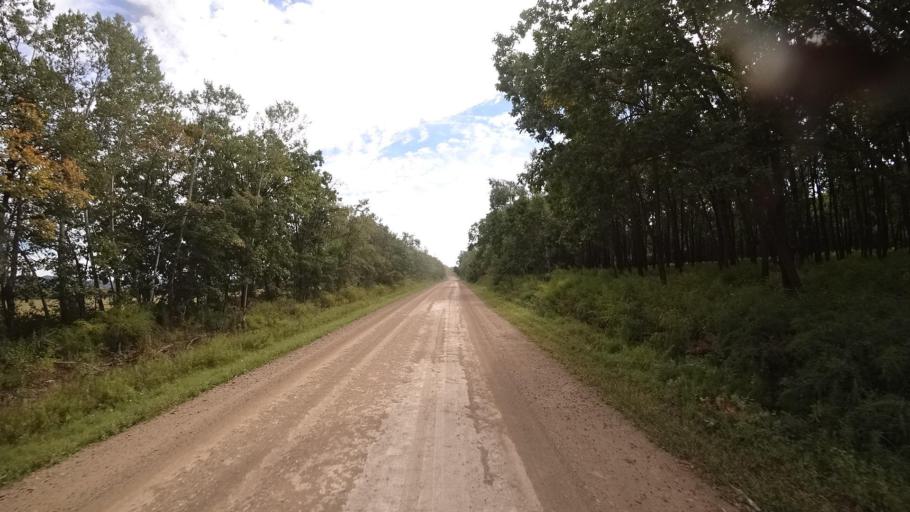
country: RU
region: Primorskiy
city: Yakovlevka
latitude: 44.5189
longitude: 133.5968
